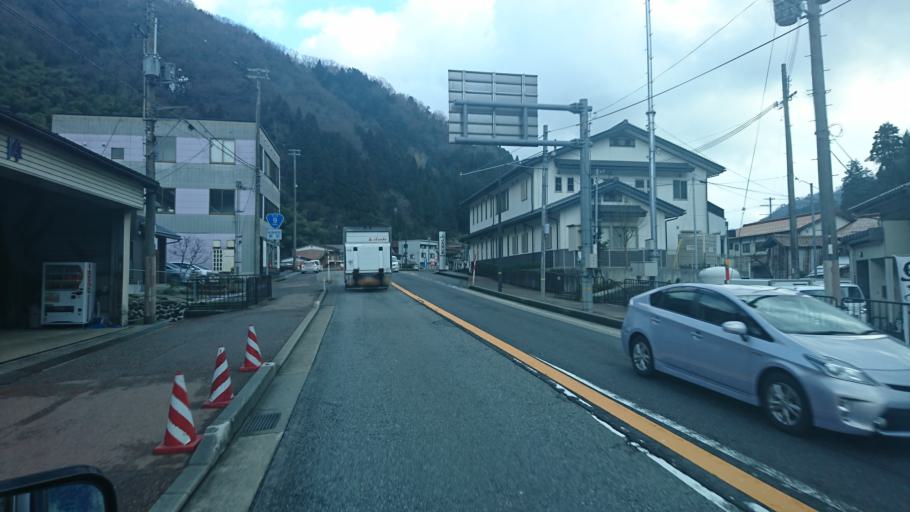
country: JP
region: Tottori
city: Tottori
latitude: 35.5607
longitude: 134.4843
